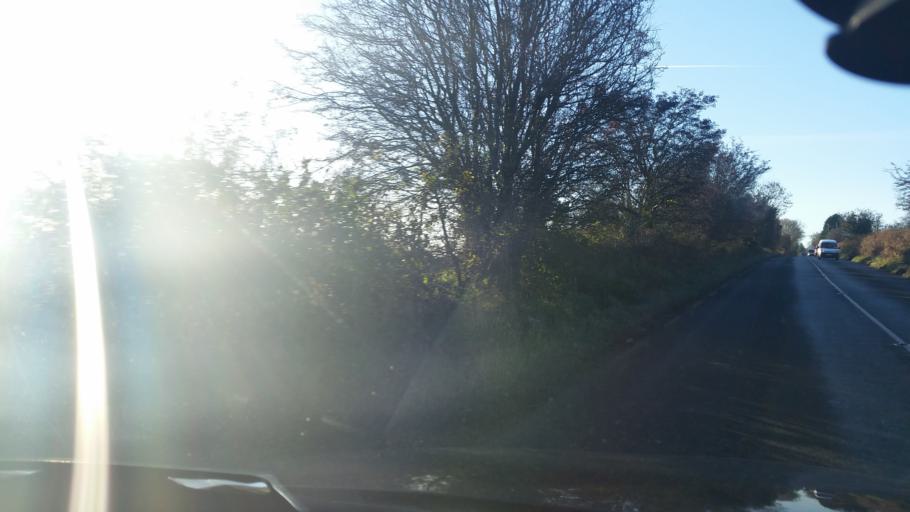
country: IE
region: Leinster
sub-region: Loch Garman
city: Gorey
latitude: 52.5824
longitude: -6.3114
